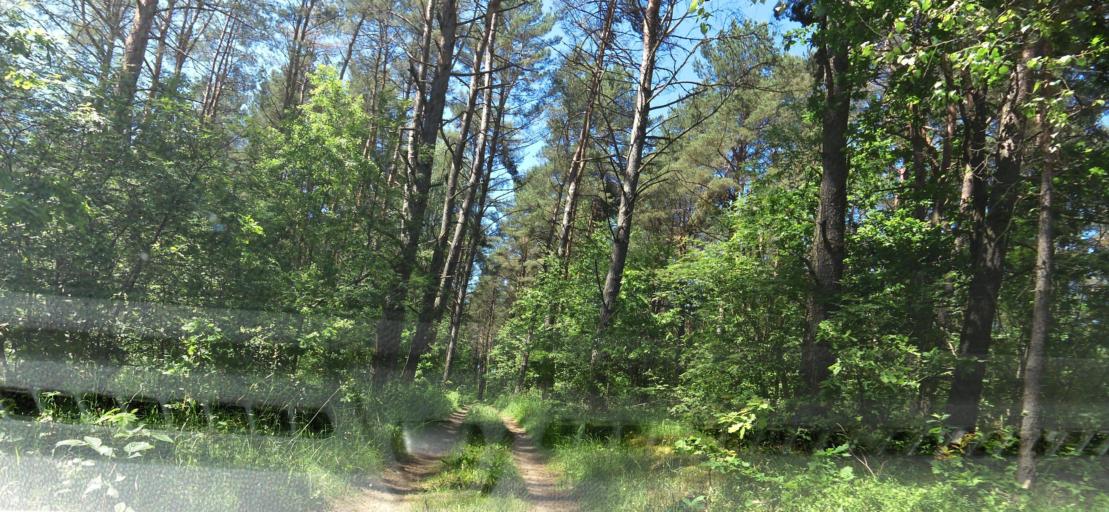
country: LT
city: Moletai
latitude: 55.0721
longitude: 25.2427
